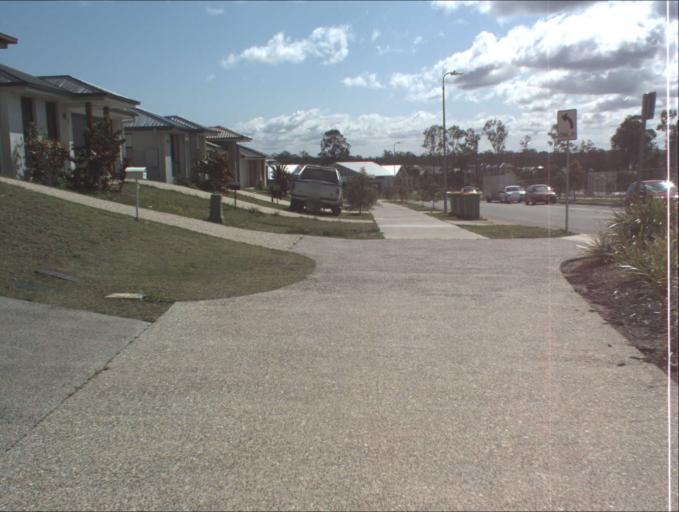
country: AU
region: Queensland
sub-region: Logan
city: Chambers Flat
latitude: -27.8051
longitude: 153.1086
